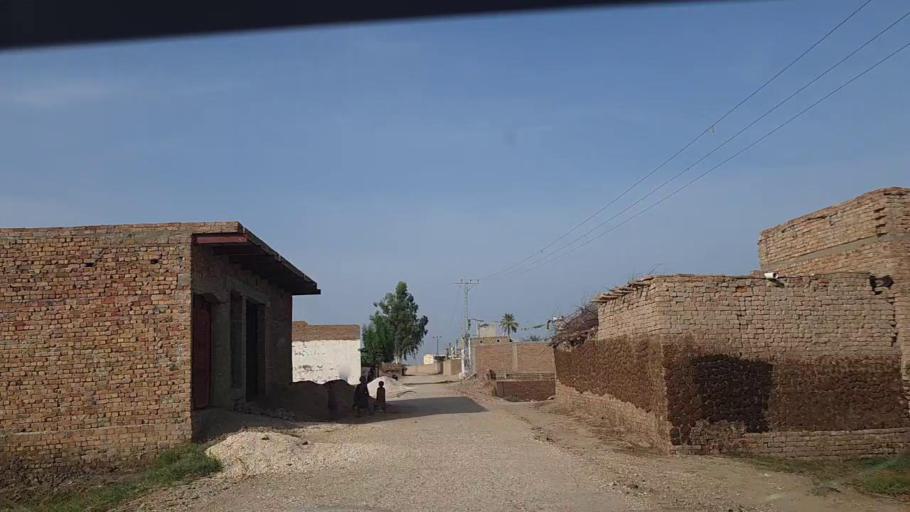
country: PK
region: Sindh
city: Ghotki
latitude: 28.0136
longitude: 69.2942
